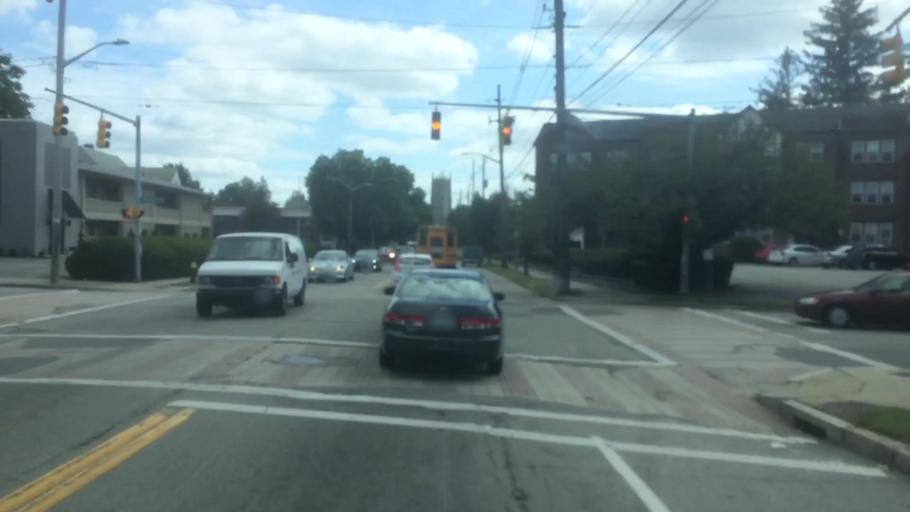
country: US
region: Rhode Island
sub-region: Providence County
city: Cranston
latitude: 41.7810
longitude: -71.4009
